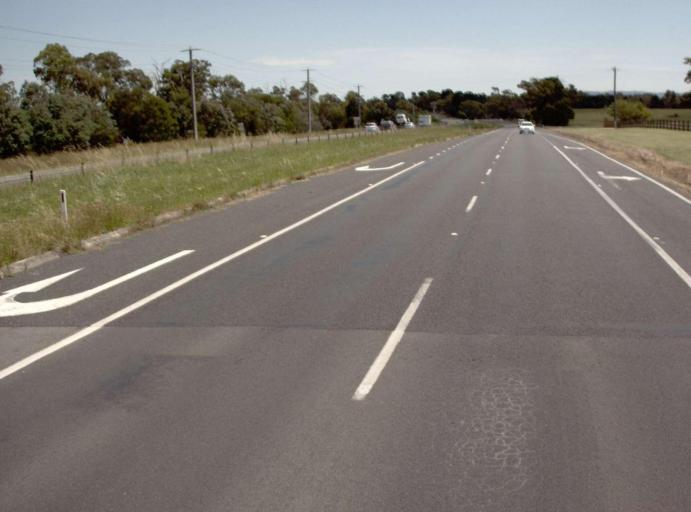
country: AU
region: Victoria
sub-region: Latrobe
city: Traralgon
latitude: -38.2095
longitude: 146.4927
